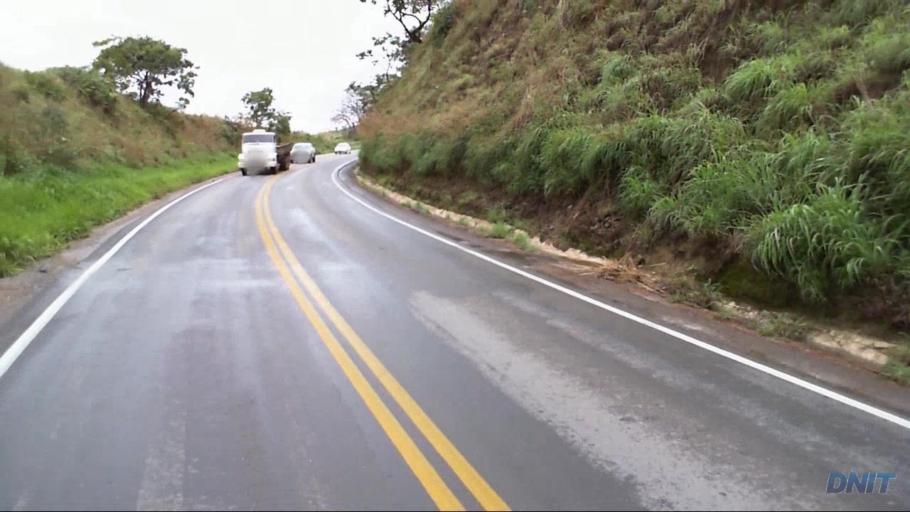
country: BR
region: Goias
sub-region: Padre Bernardo
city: Padre Bernardo
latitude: -15.4835
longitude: -48.2351
